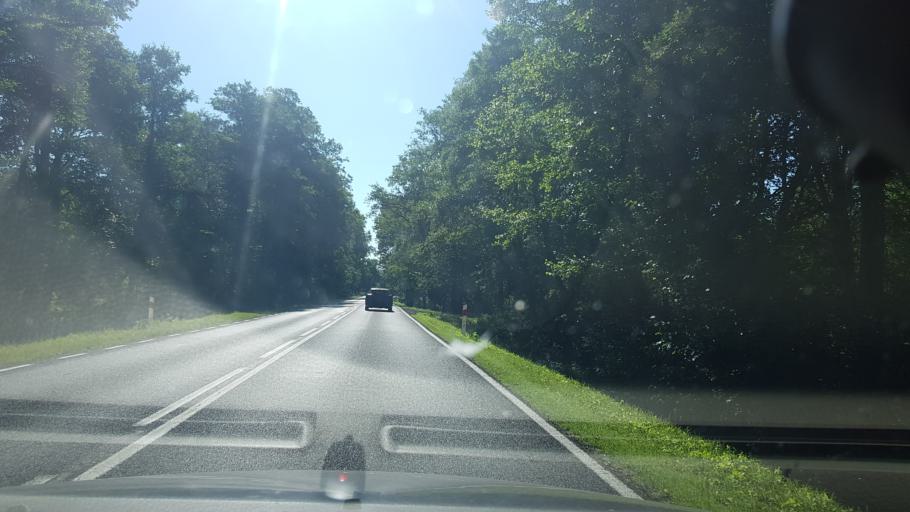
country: PL
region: Masovian Voivodeship
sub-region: Powiat wyszkowski
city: Wyszkow
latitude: 52.5867
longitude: 21.5170
